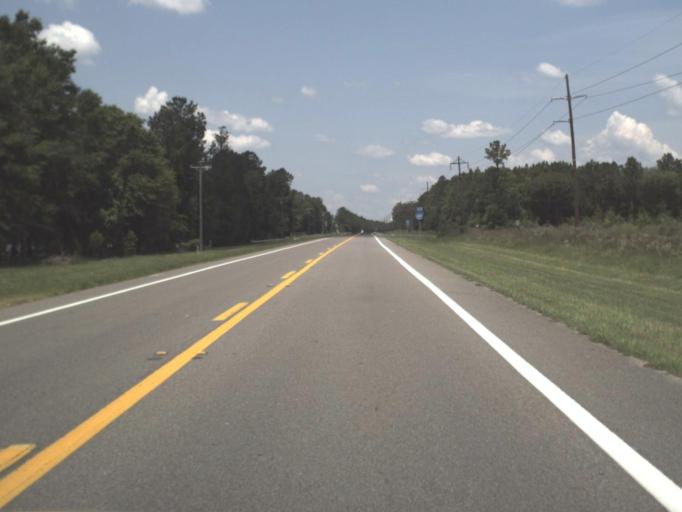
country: US
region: Florida
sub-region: Union County
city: Lake Butler
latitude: 30.0033
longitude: -82.2840
